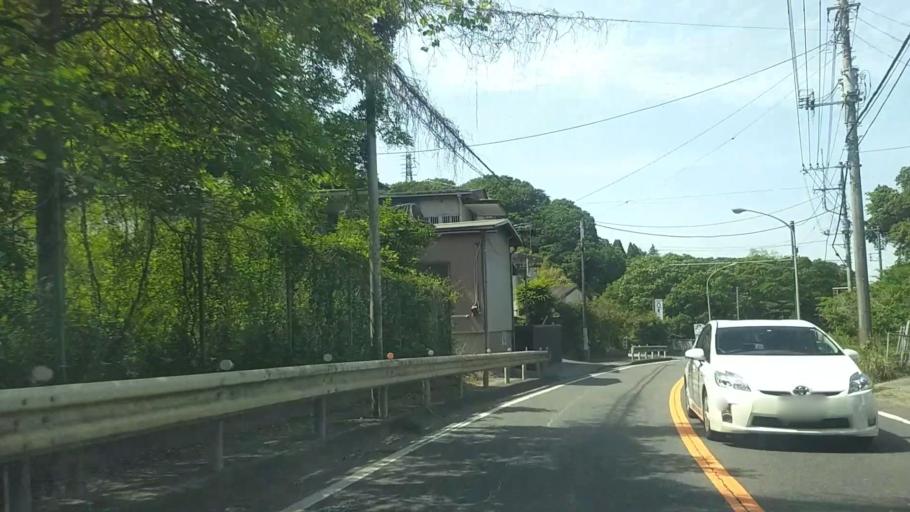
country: JP
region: Kanagawa
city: Kamakura
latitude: 35.3413
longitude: 139.5822
